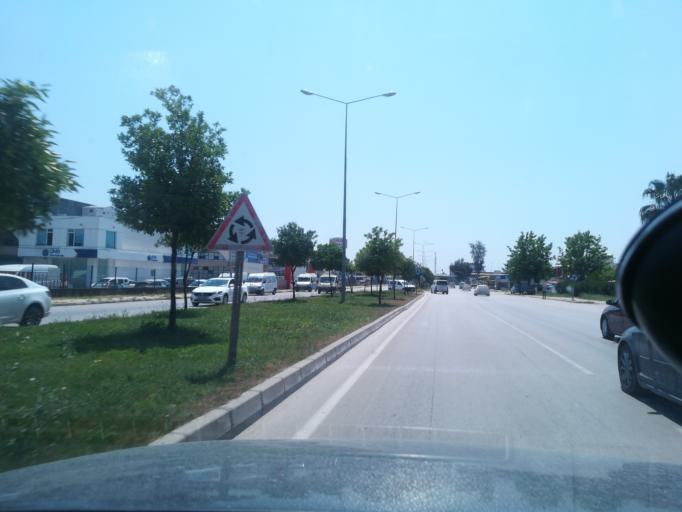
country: TR
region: Adana
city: Seyhan
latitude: 36.9936
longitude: 35.2522
